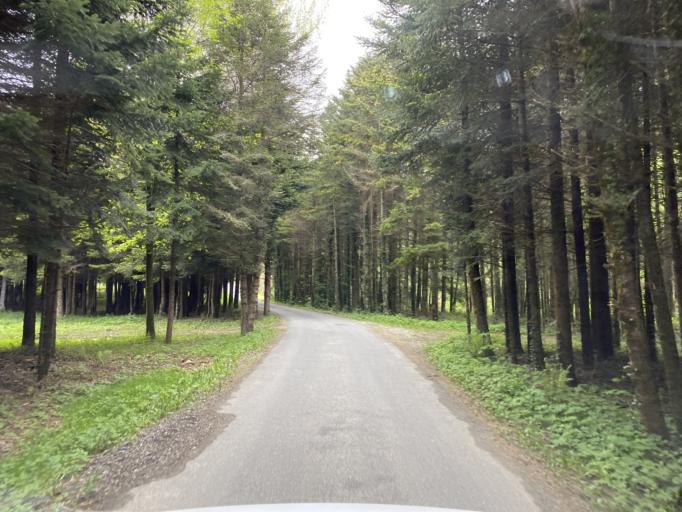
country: AT
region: Styria
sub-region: Politischer Bezirk Weiz
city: Koglhof
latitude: 47.3125
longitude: 15.6865
